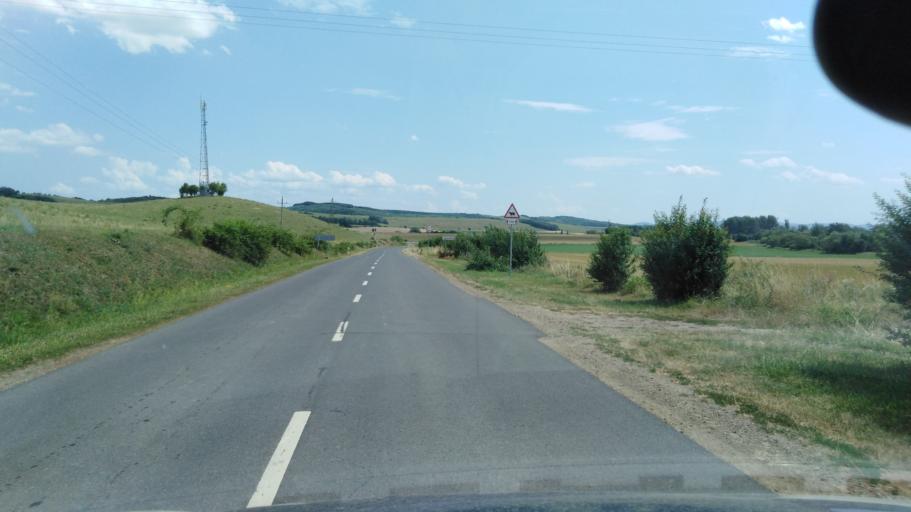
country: HU
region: Nograd
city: Szecseny
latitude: 48.1759
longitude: 19.5259
